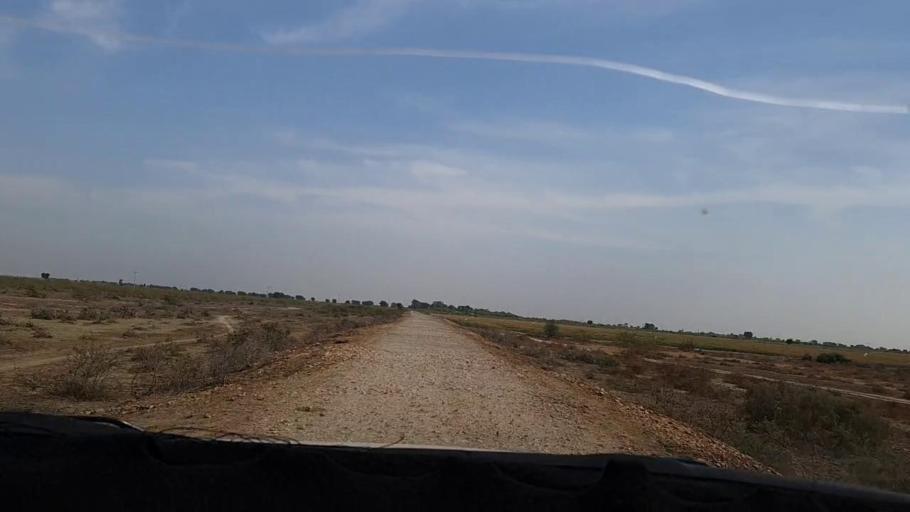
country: PK
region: Sindh
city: Pithoro
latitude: 25.5403
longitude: 69.3342
